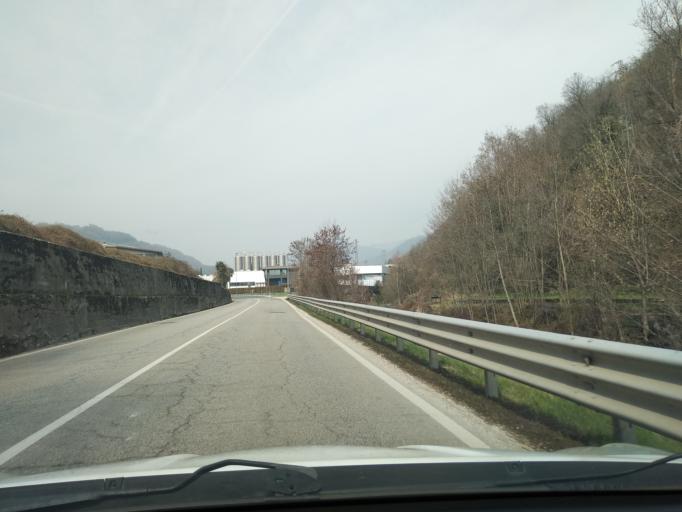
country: IT
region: Veneto
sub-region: Provincia di Vicenza
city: Chiampo
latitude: 45.5599
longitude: 11.2694
